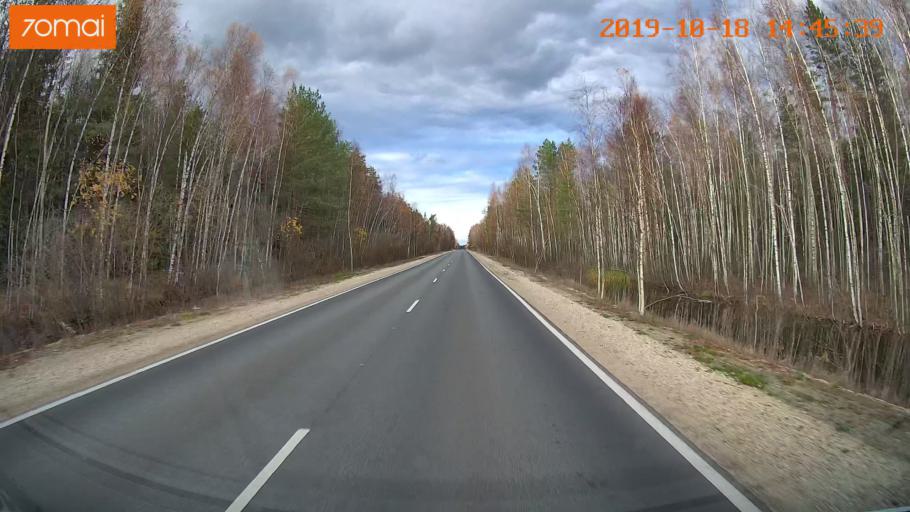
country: RU
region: Vladimir
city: Velikodvorskiy
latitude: 55.3585
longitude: 40.6793
